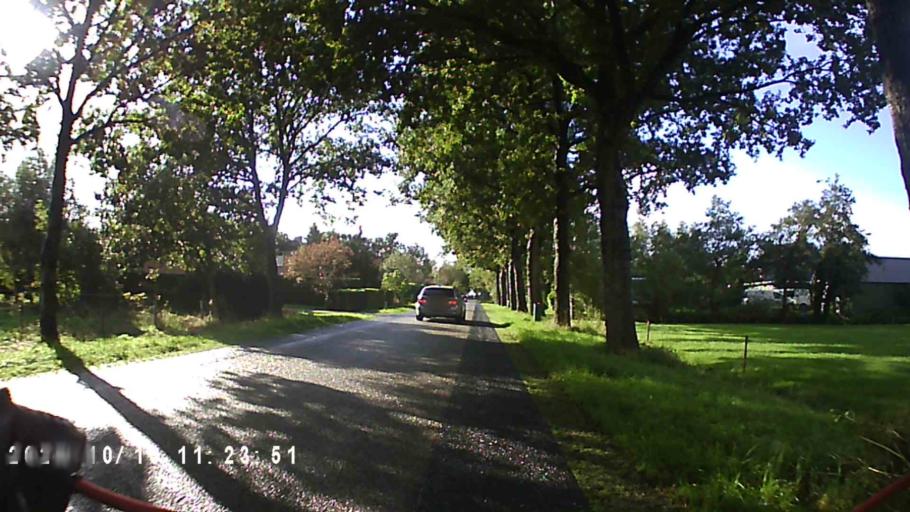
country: NL
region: Friesland
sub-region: Gemeente Smallingerland
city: Drachtstercompagnie
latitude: 53.0888
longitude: 6.1762
